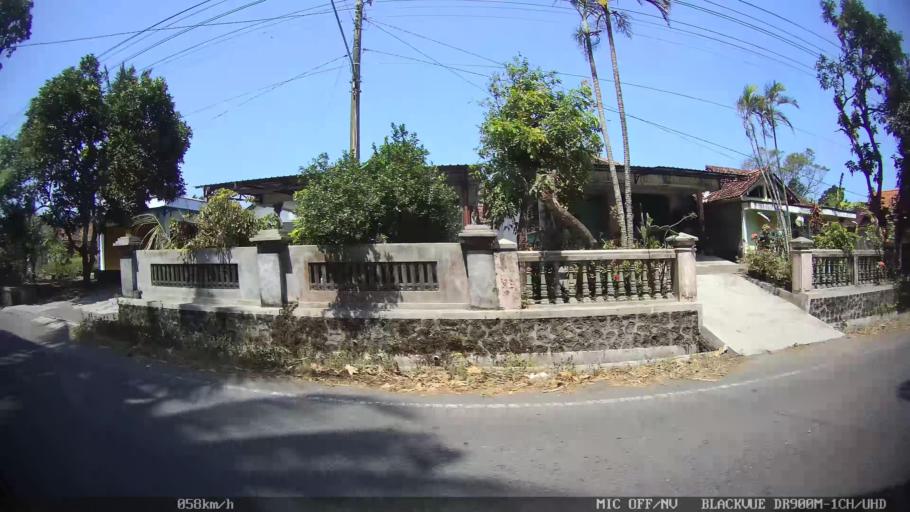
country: ID
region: Daerah Istimewa Yogyakarta
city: Srandakan
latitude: -7.9165
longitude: 110.1032
